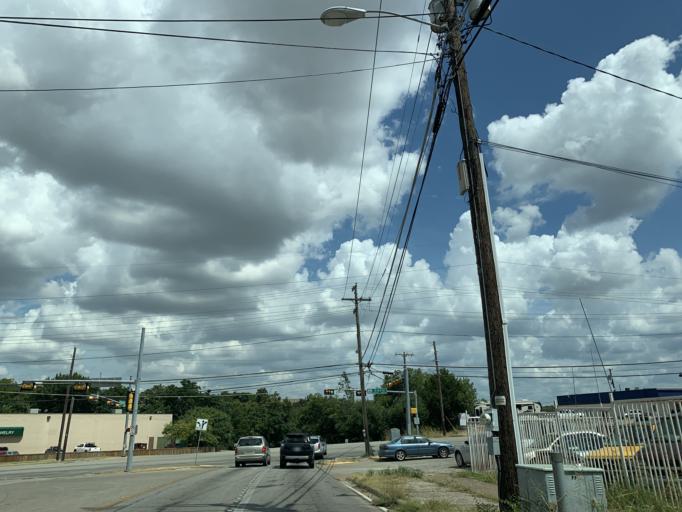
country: US
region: Texas
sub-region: Dallas County
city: Cockrell Hill
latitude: 32.7490
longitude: -96.8626
